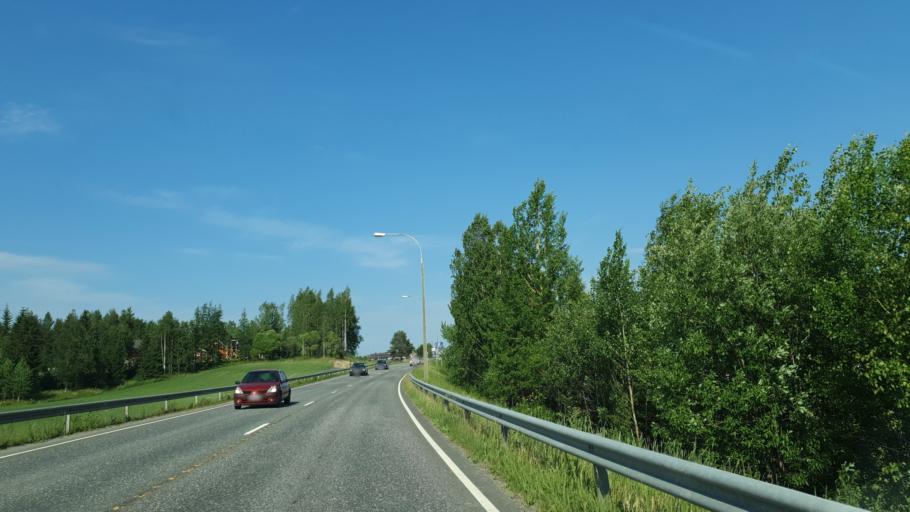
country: FI
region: Northern Savo
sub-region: Kuopio
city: Siilinjaervi
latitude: 63.1404
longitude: 27.8546
